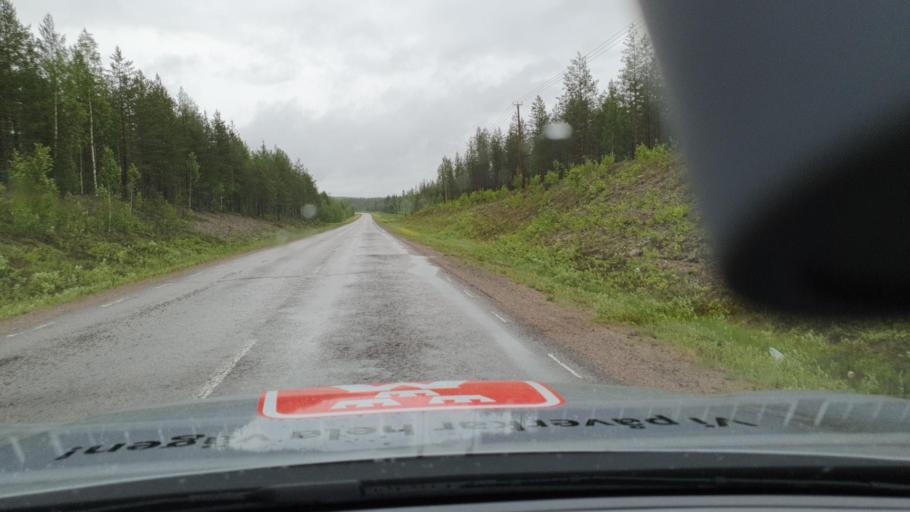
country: SE
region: Norrbotten
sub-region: Overkalix Kommun
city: OEverkalix
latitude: 66.4422
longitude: 23.1805
